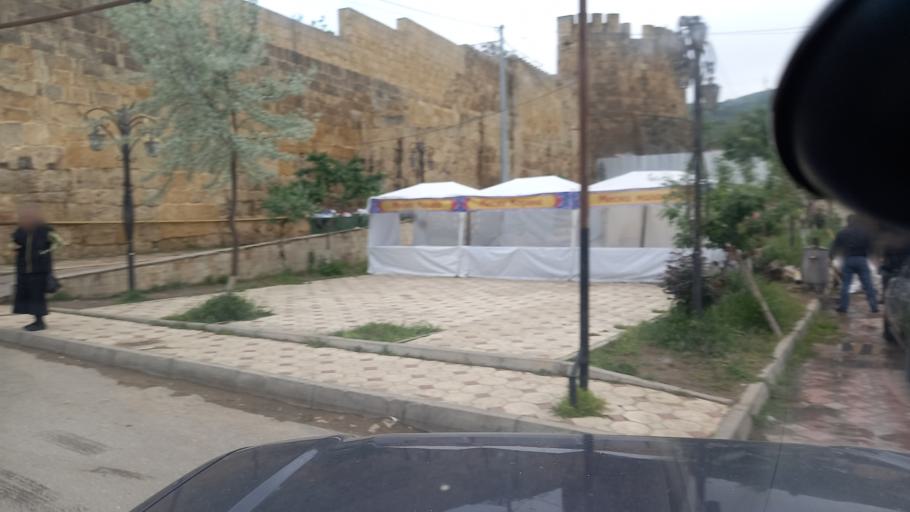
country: RU
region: Dagestan
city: Derbent
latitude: 42.0577
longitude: 48.2814
